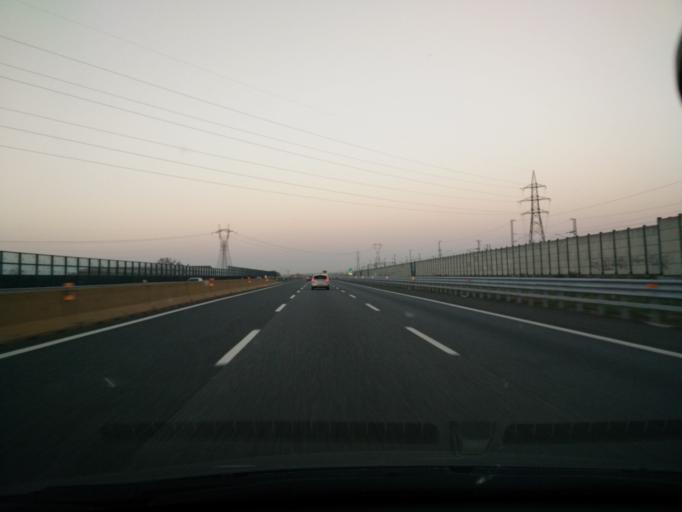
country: IT
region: Piedmont
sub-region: Provincia di Vercelli
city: Cigliano
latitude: 45.2807
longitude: 8.0288
